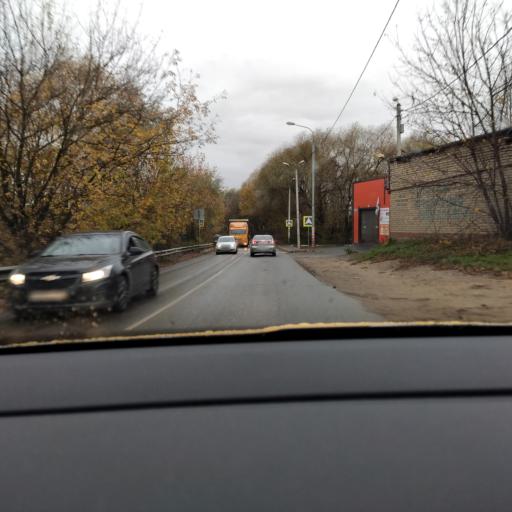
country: RU
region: Moskovskaya
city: Ivanteyevka
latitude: 55.9639
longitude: 37.9378
